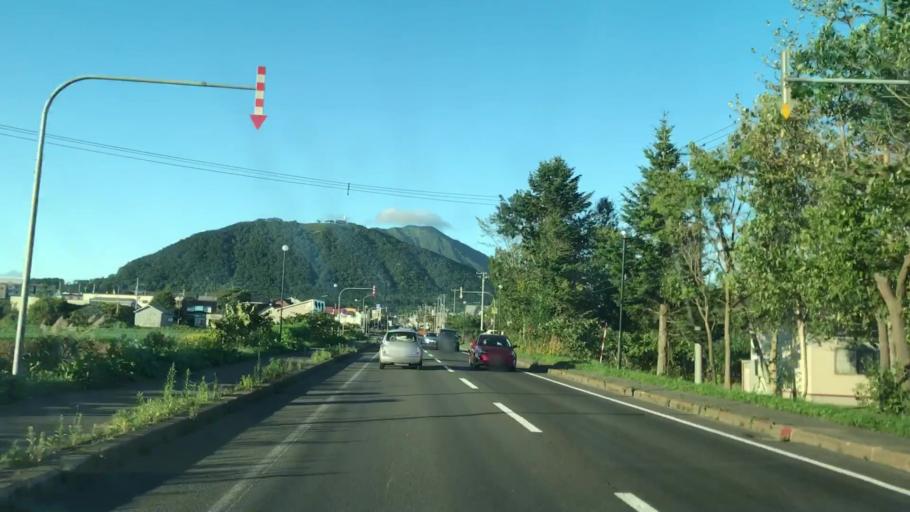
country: JP
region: Hokkaido
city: Niseko Town
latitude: 42.7308
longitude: 140.8708
